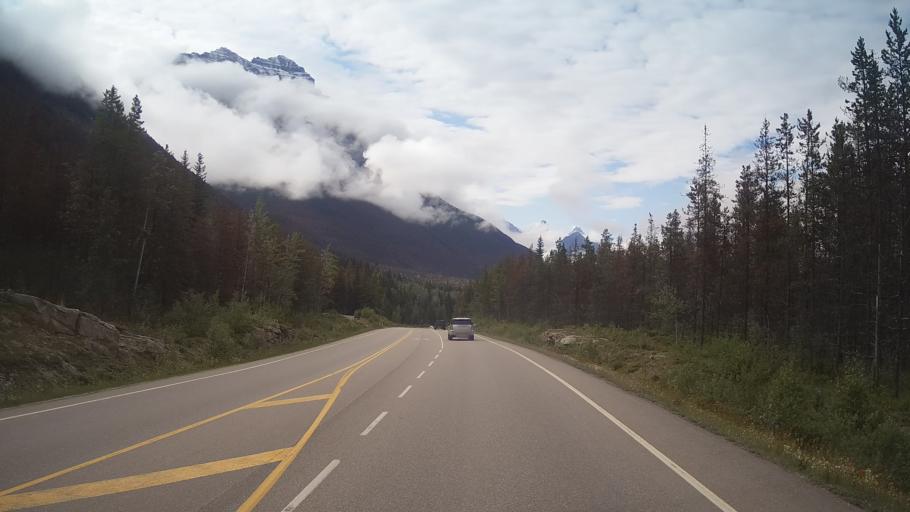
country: CA
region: Alberta
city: Jasper Park Lodge
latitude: 52.6963
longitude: -117.8682
